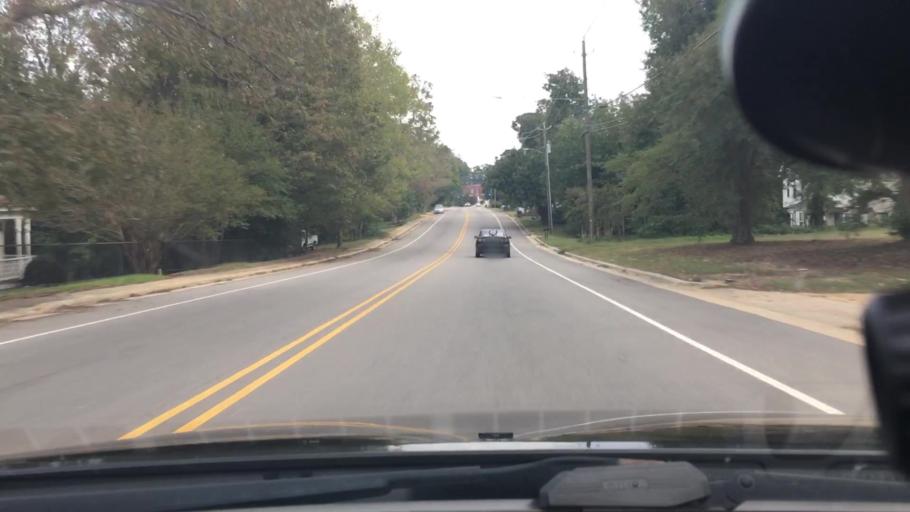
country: US
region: North Carolina
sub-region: Moore County
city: Carthage
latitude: 35.3511
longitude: -79.4217
